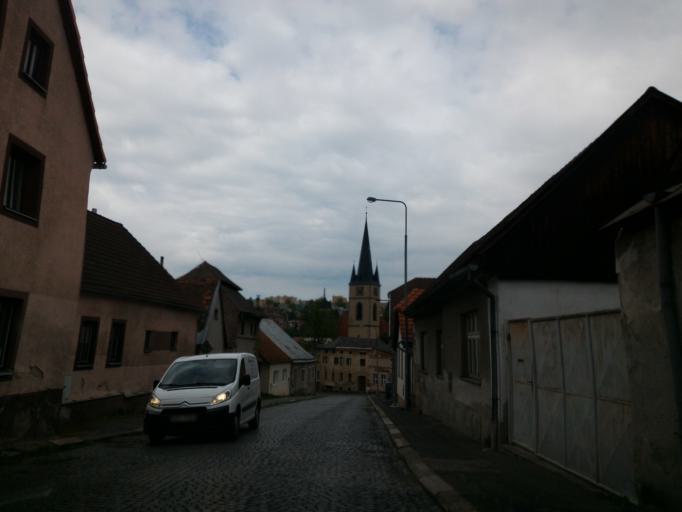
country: CZ
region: Vysocina
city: Ledec nad Sazavou
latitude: 49.6939
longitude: 15.2811
